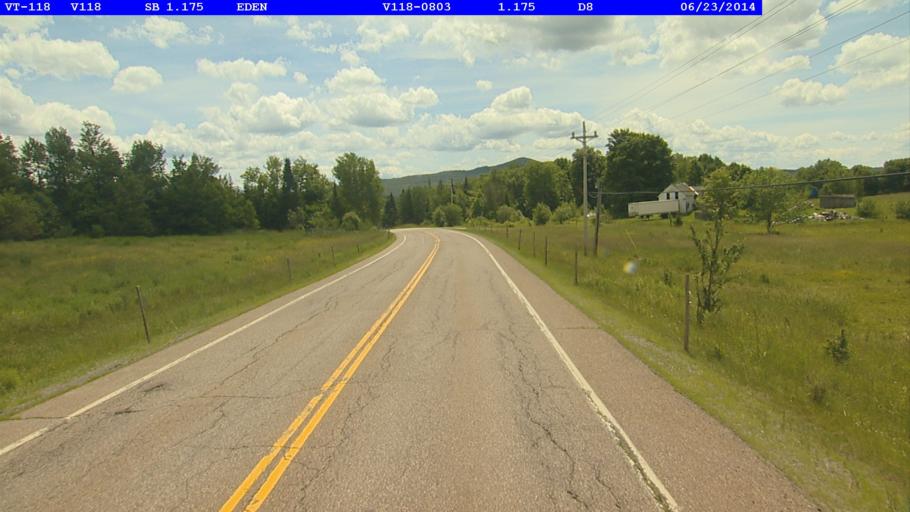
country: US
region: Vermont
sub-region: Lamoille County
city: Hyde Park
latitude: 44.7212
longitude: -72.5594
